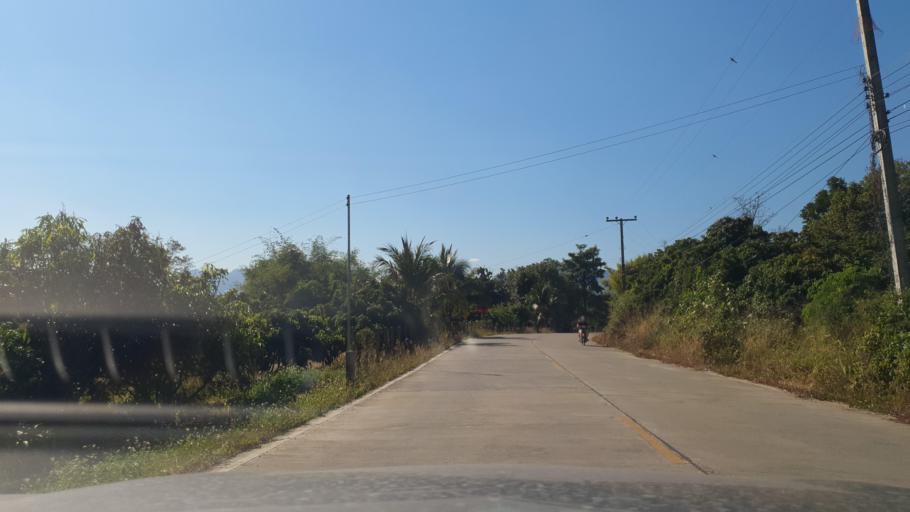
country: TH
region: Chiang Mai
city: Mae Wang
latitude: 18.6778
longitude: 98.8235
